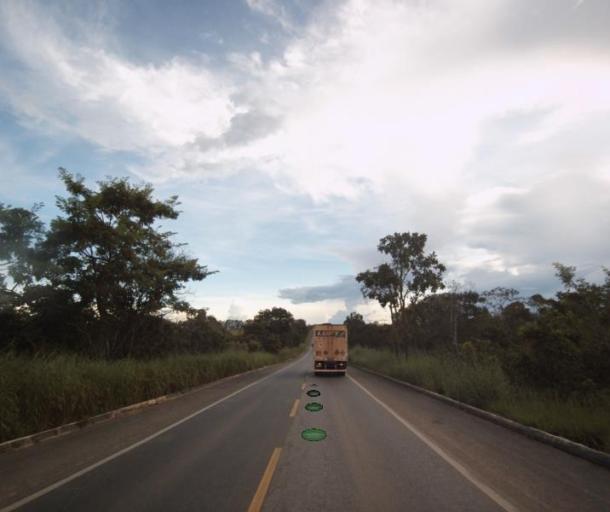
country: BR
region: Goias
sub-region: Uruacu
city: Uruacu
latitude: -14.1323
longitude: -49.1119
